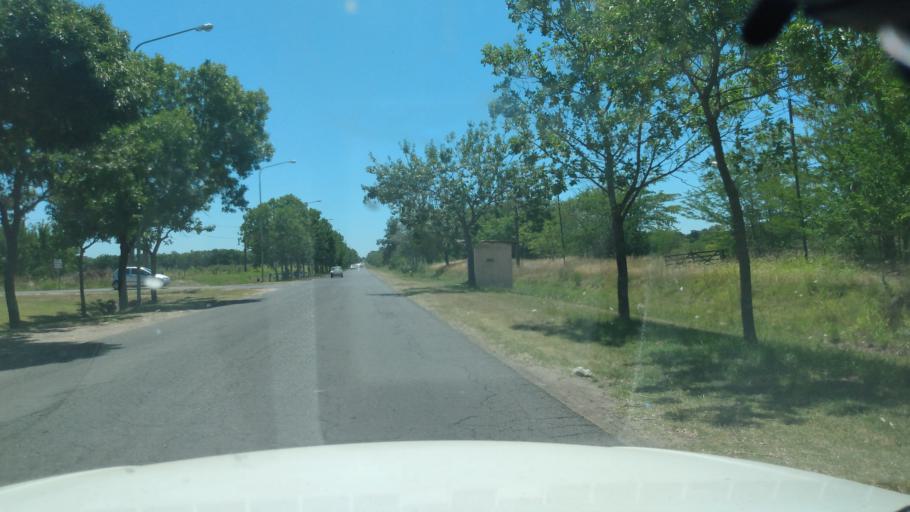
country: AR
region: Buenos Aires
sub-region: Partido de Lujan
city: Lujan
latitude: -34.5791
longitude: -59.1704
